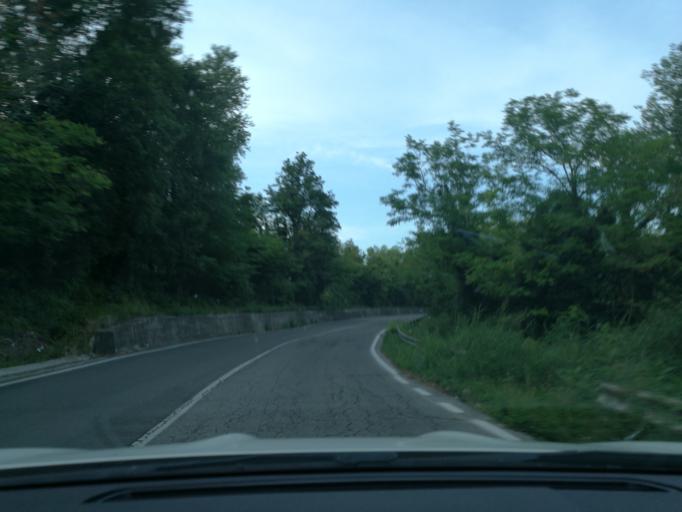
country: IT
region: Umbria
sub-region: Provincia di Terni
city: San Gemini
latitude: 42.6284
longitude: 12.5520
